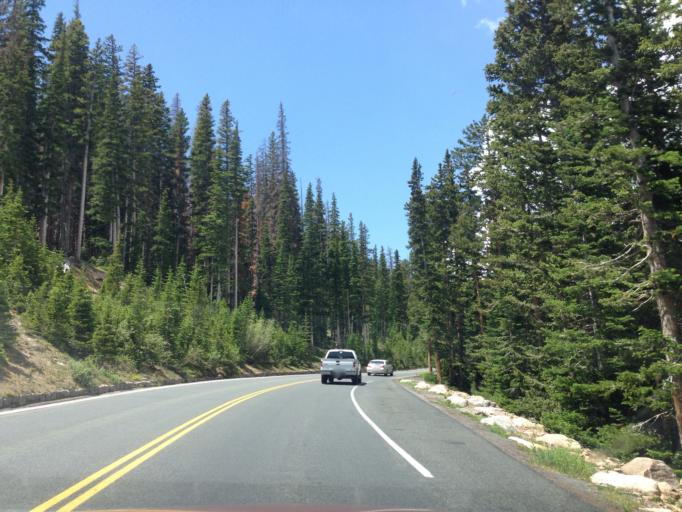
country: US
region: Colorado
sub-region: Larimer County
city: Estes Park
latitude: 40.3863
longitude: -105.6563
